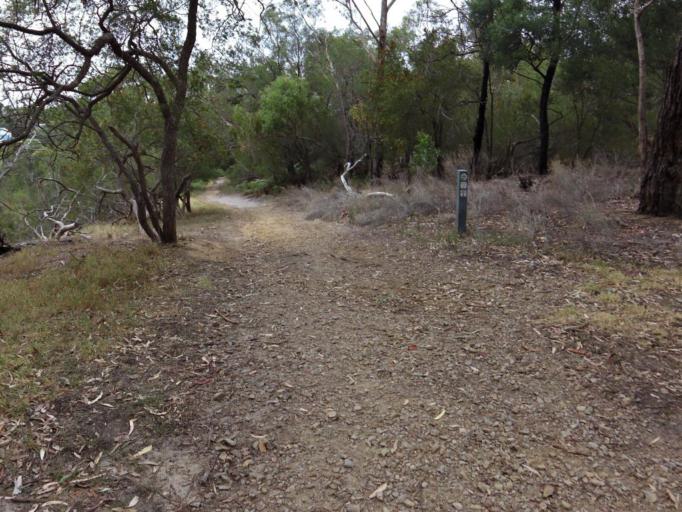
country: AU
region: Victoria
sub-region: Frankston
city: Frankston
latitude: -38.1658
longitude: 145.1104
